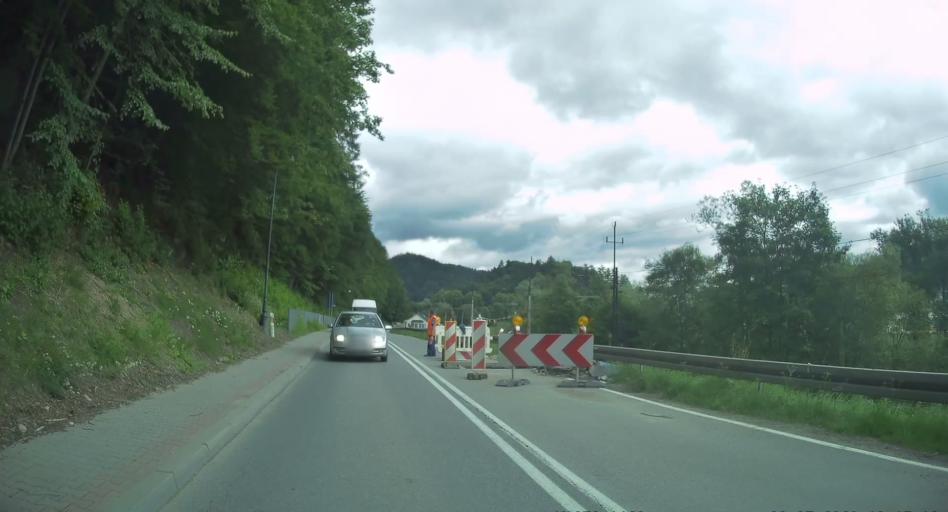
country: PL
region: Lesser Poland Voivodeship
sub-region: Powiat nowosadecki
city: Muszyna
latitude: 49.3501
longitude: 20.8839
